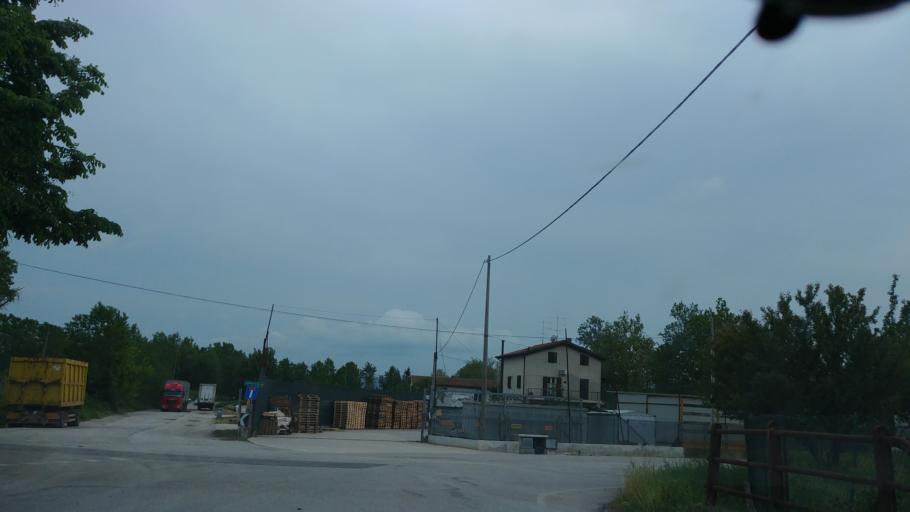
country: IT
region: The Marches
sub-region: Provincia di Pesaro e Urbino
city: Villa Ceccolini
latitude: 43.8953
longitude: 12.8373
